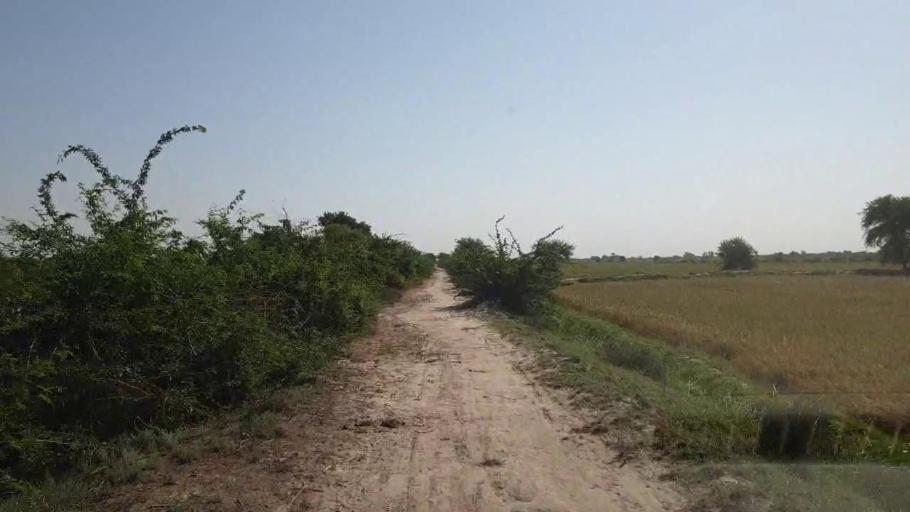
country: PK
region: Sindh
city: Kadhan
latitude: 24.5998
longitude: 69.0047
